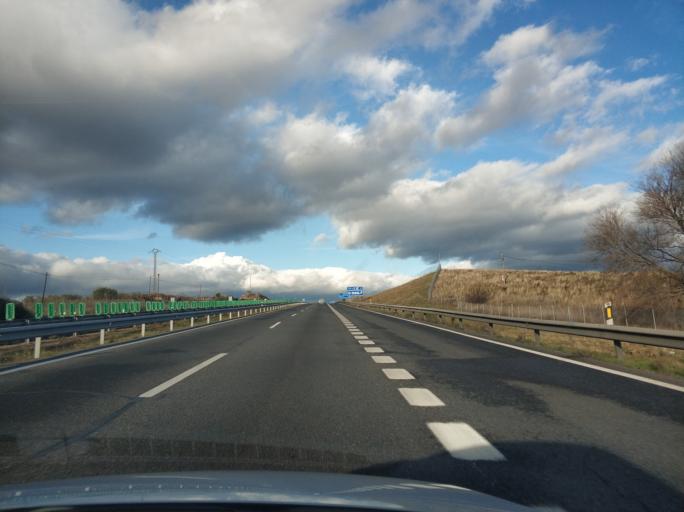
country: ES
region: Madrid
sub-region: Provincia de Madrid
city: El Molar
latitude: 40.7053
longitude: -3.5837
